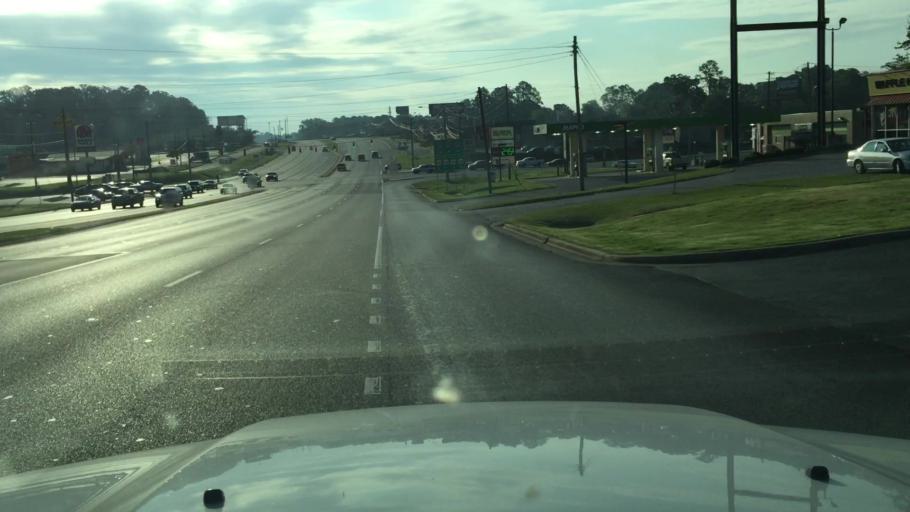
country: US
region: Alabama
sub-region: Tuscaloosa County
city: Northport
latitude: 33.2394
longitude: -87.5783
